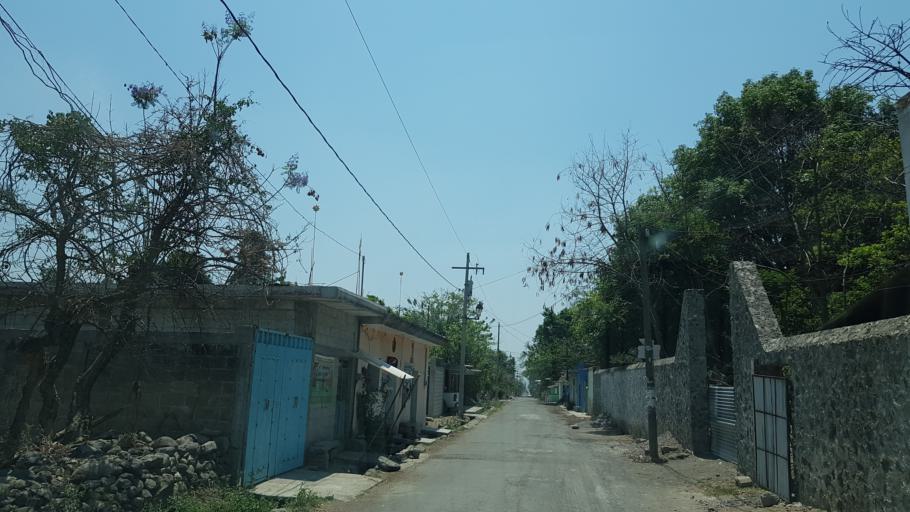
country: MX
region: Puebla
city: Huaquechula
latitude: 18.7767
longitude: -98.5450
